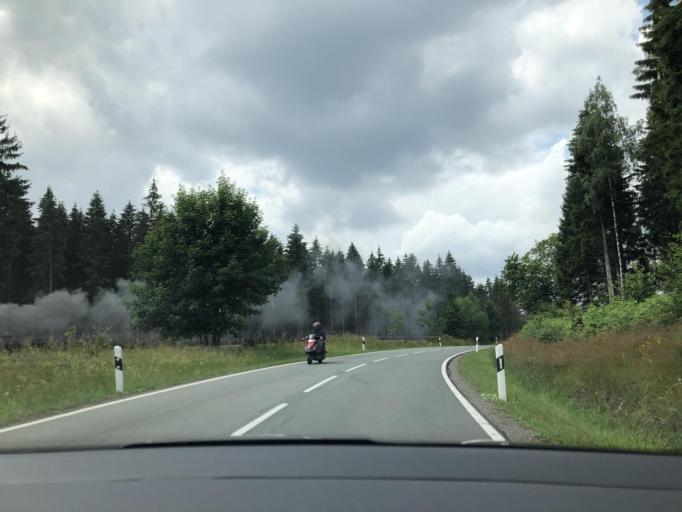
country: DE
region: Saxony-Anhalt
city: Benneckenstein
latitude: 51.7563
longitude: 10.7120
